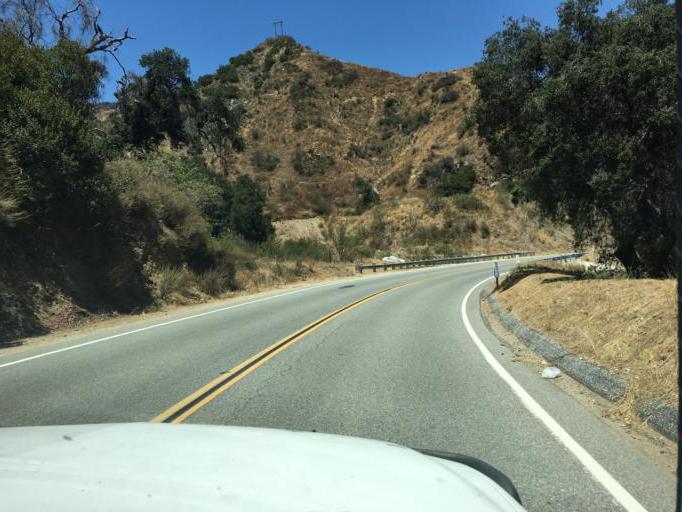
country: US
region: California
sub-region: Los Angeles County
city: Glendora
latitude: 34.1925
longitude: -117.8658
